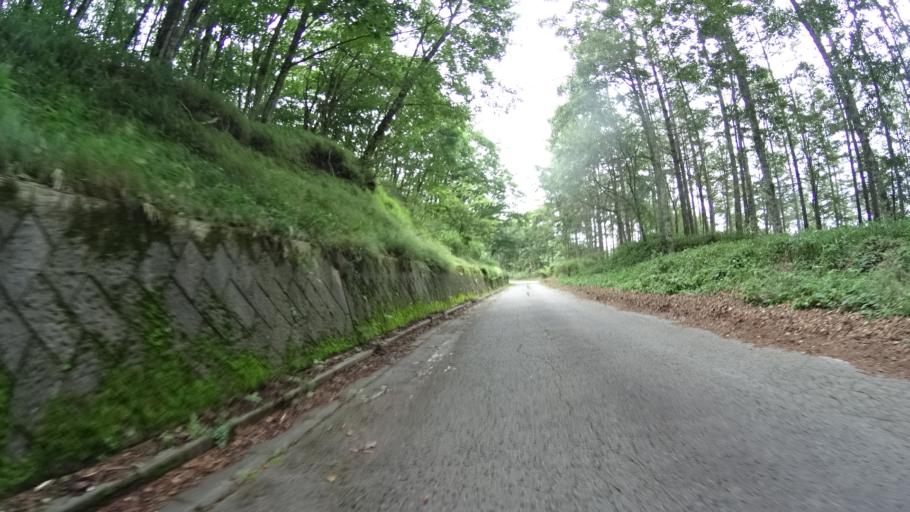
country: JP
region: Yamanashi
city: Kofu-shi
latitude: 35.8228
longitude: 138.5552
